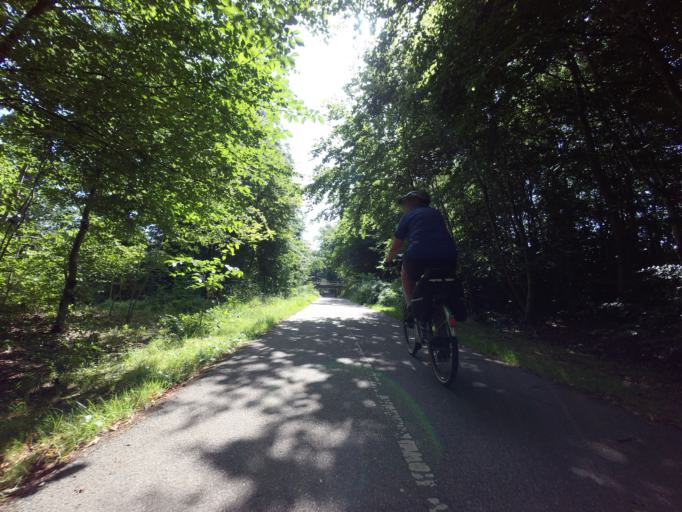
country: GB
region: Scotland
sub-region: Highland
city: Inverness
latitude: 57.4866
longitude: -4.1403
